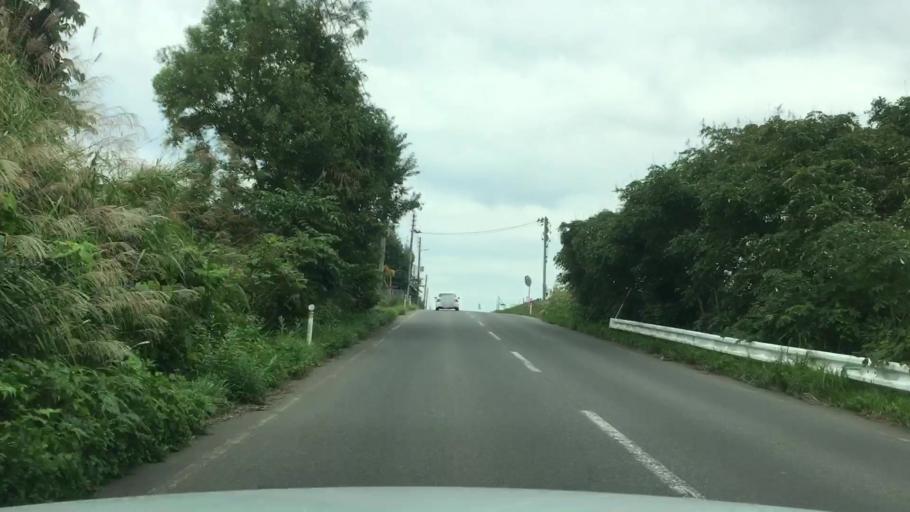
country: JP
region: Aomori
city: Hirosaki
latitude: 40.6529
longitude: 140.4215
